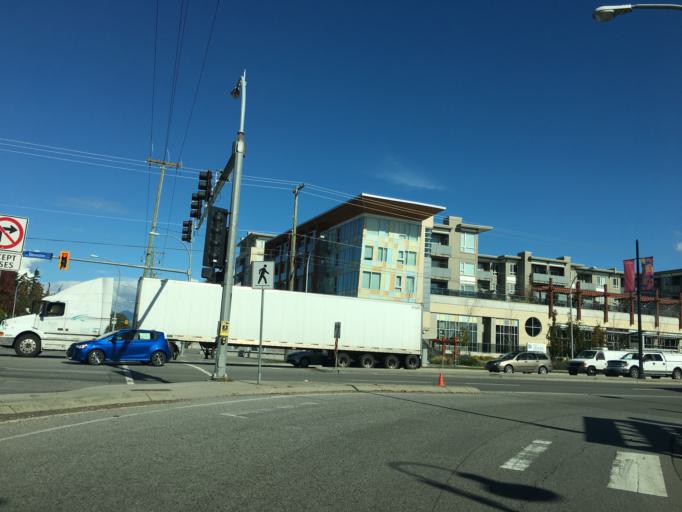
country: CA
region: British Columbia
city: Ladner
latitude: 49.1331
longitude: -123.0920
